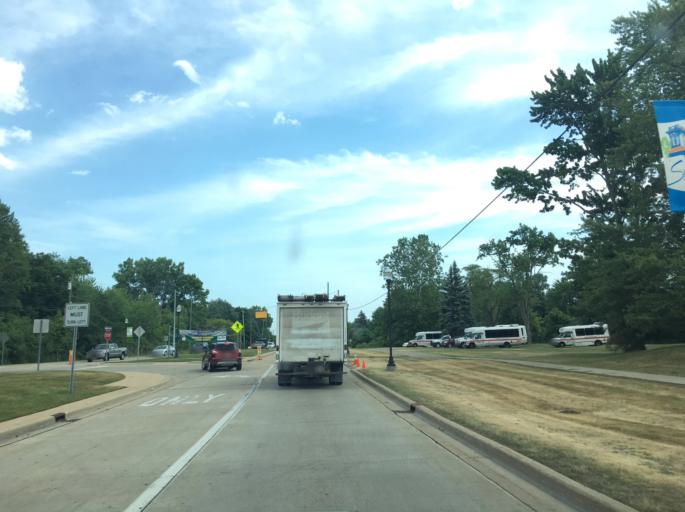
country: US
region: Michigan
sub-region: Macomb County
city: Sterling Heights
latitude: 42.5904
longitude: -83.0095
